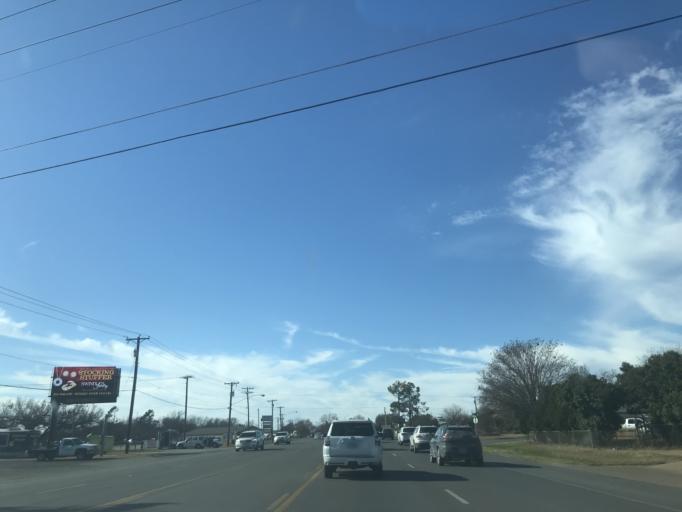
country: US
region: Texas
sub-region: Erath County
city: Stephenville
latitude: 32.2068
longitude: -98.2222
